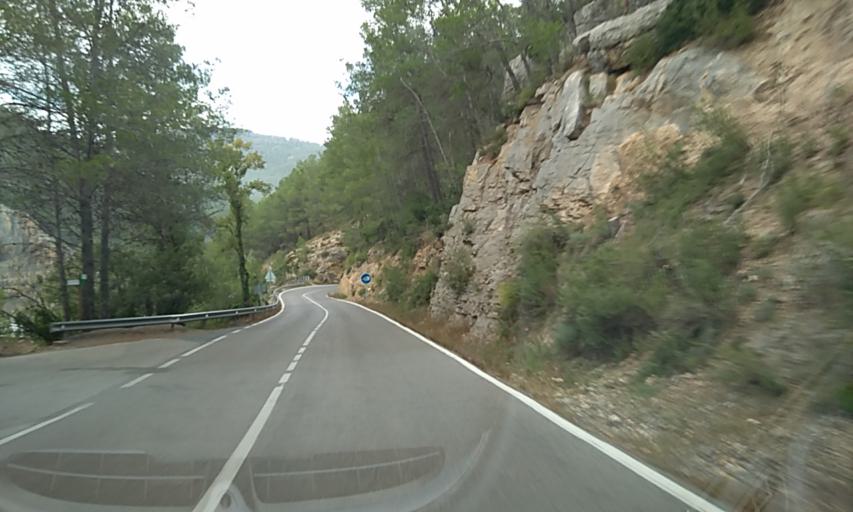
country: ES
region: Valencia
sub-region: Provincia de Castello
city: Montanejos
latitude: 40.0842
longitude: -0.5425
